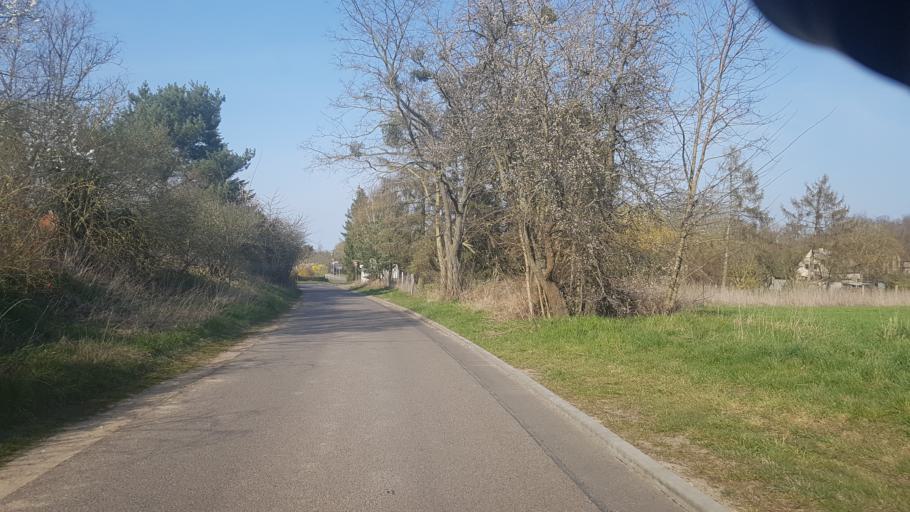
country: DE
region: Brandenburg
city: Gerswalde
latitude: 53.2137
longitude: 13.7863
